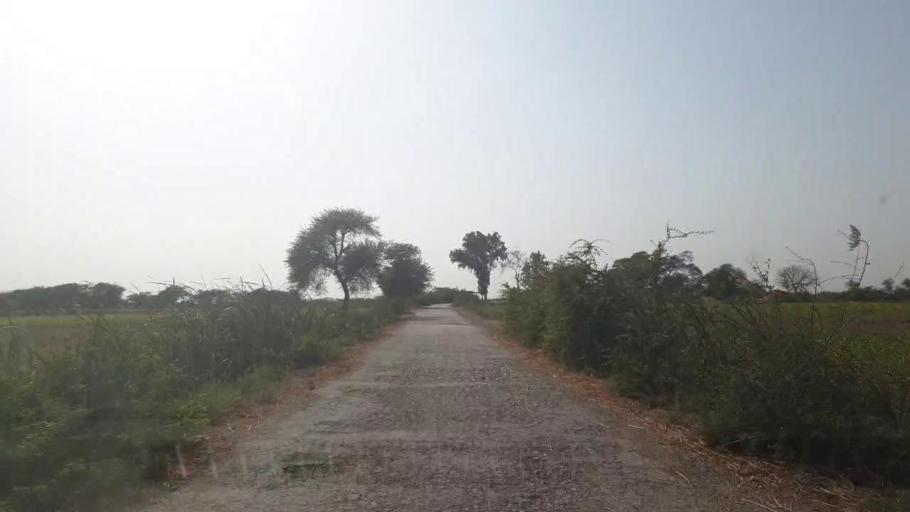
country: PK
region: Sindh
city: Kario
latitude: 24.5764
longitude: 68.4981
